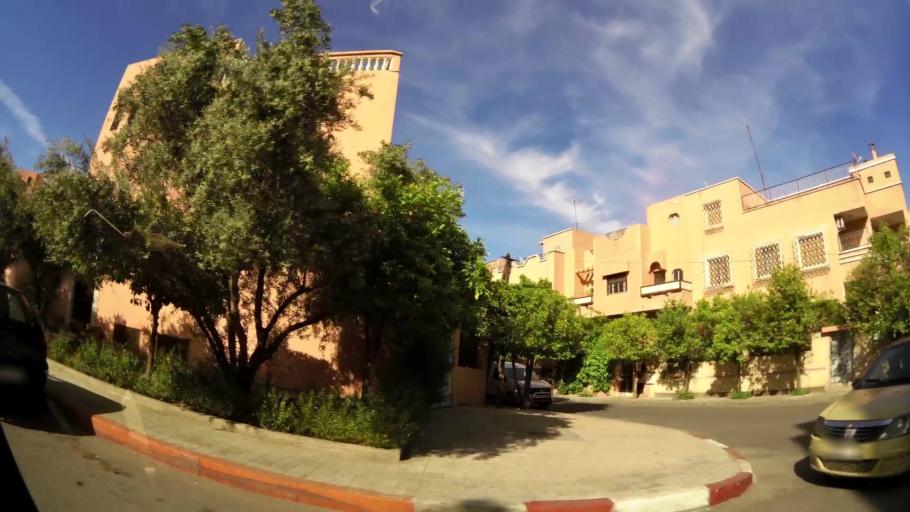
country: MA
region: Marrakech-Tensift-Al Haouz
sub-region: Marrakech
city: Marrakesh
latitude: 31.6539
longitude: -8.0090
